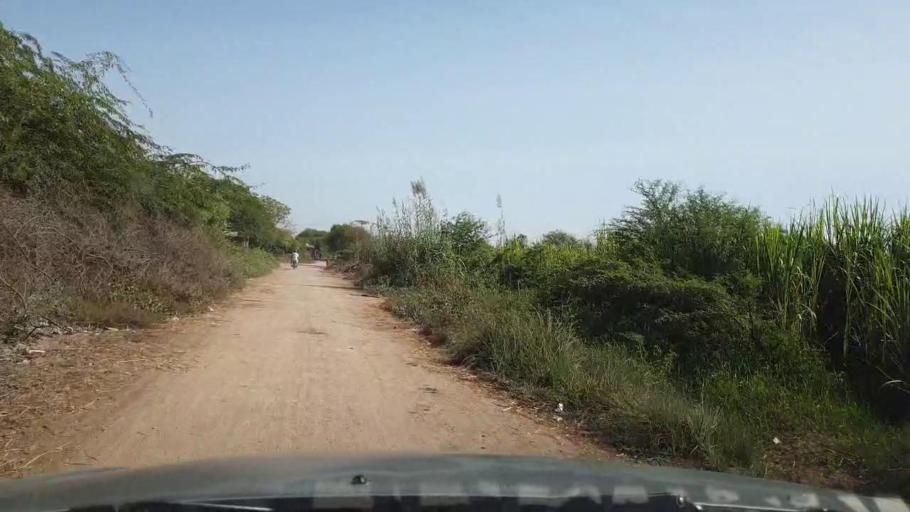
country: PK
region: Sindh
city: Bulri
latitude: 25.0208
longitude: 68.3076
